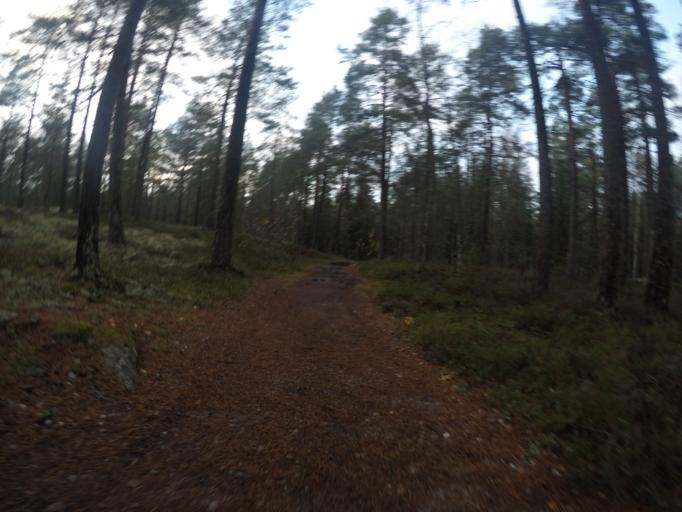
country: SE
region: Soedermanland
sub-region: Eskilstuna Kommun
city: Eskilstuna
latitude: 59.3411
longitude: 16.5200
